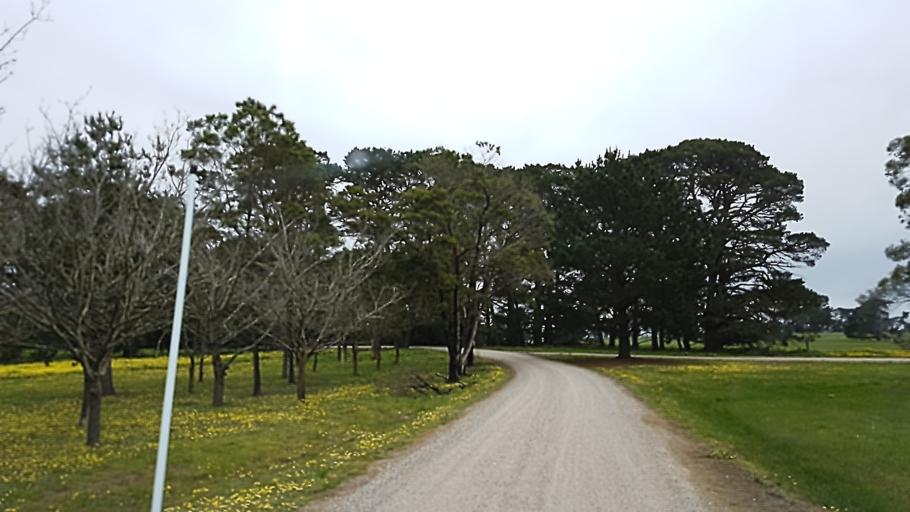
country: AU
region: Victoria
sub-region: Ballarat North
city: Mount Clear
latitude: -37.7771
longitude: 143.9843
